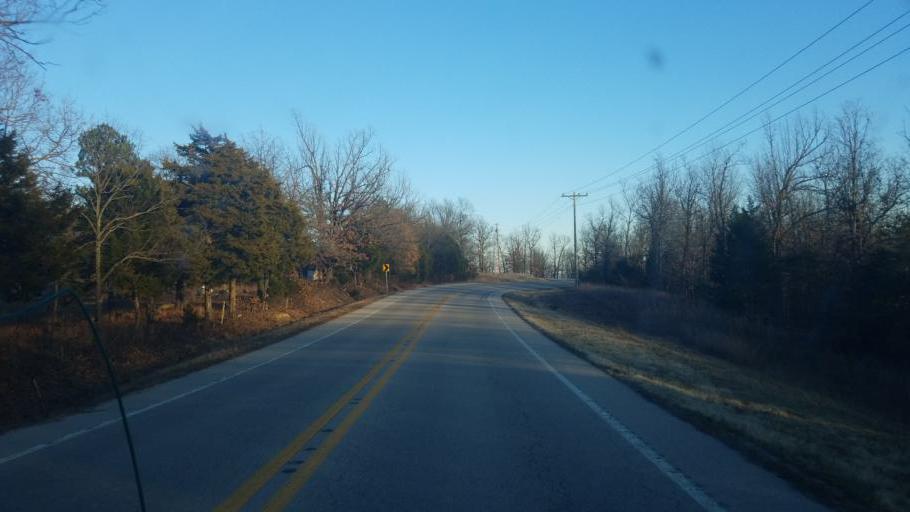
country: US
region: Arkansas
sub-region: Baxter County
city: Mountain Home
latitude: 36.3844
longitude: -92.1550
